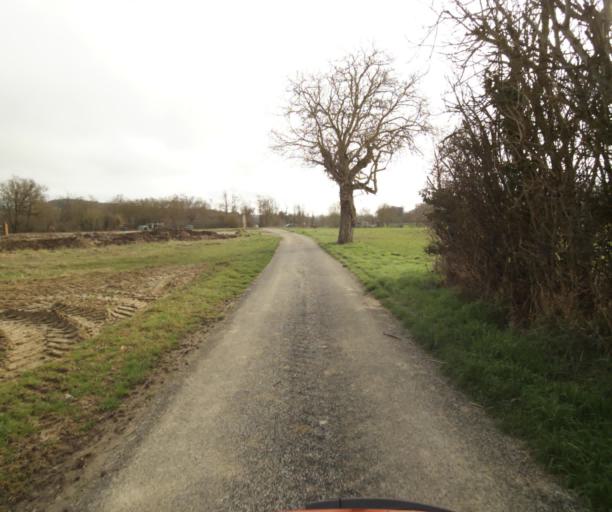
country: FR
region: Languedoc-Roussillon
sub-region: Departement de l'Aude
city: Belpech
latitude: 43.1855
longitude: 1.7336
